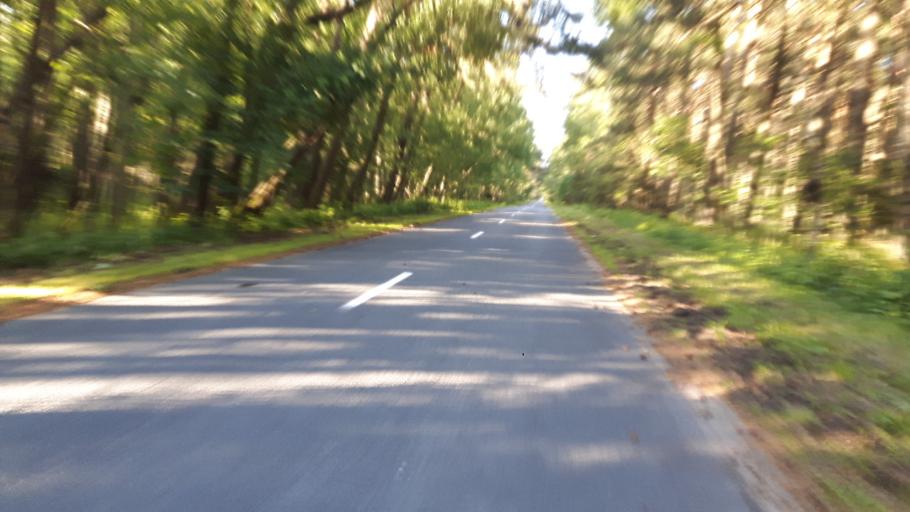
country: LT
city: Nida
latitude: 55.2540
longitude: 20.9310
